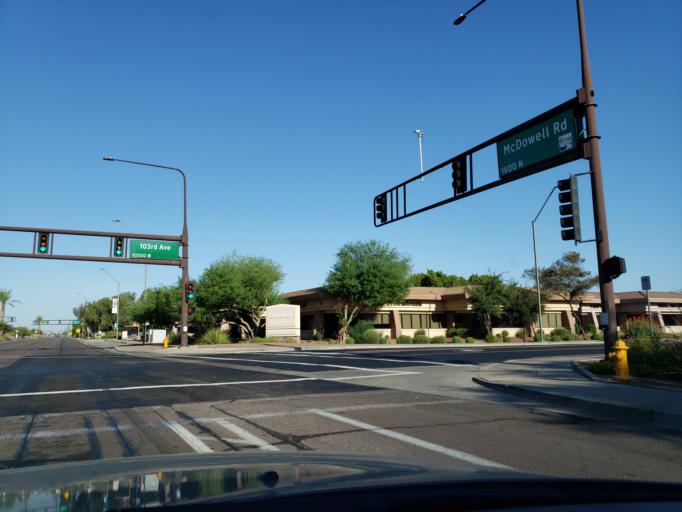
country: US
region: Arizona
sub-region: Maricopa County
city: Tolleson
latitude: 33.4647
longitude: -112.2810
